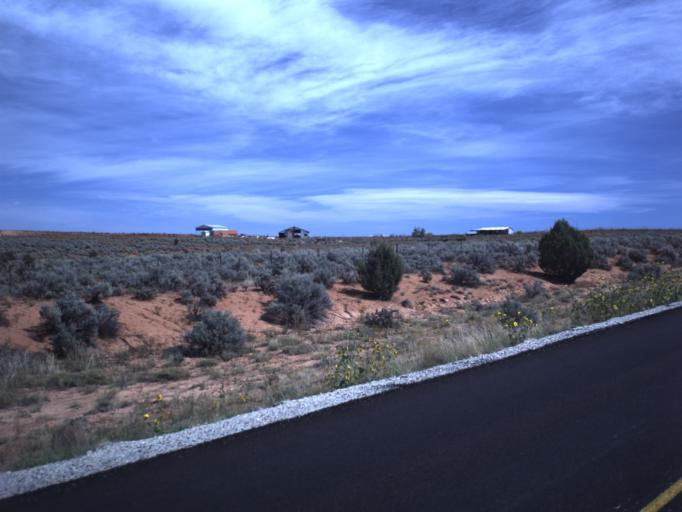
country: US
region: Utah
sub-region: San Juan County
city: Blanding
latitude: 37.5736
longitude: -109.4970
